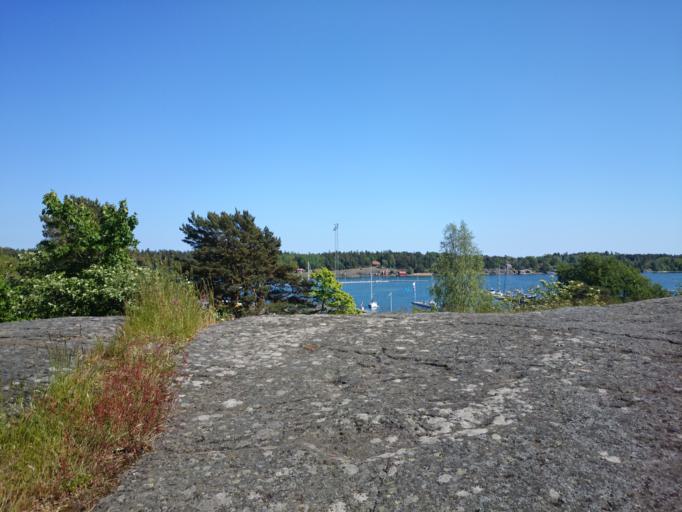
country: SE
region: Stockholm
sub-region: Nynashamns Kommun
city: Nynashamn
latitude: 58.9026
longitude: 17.9507
